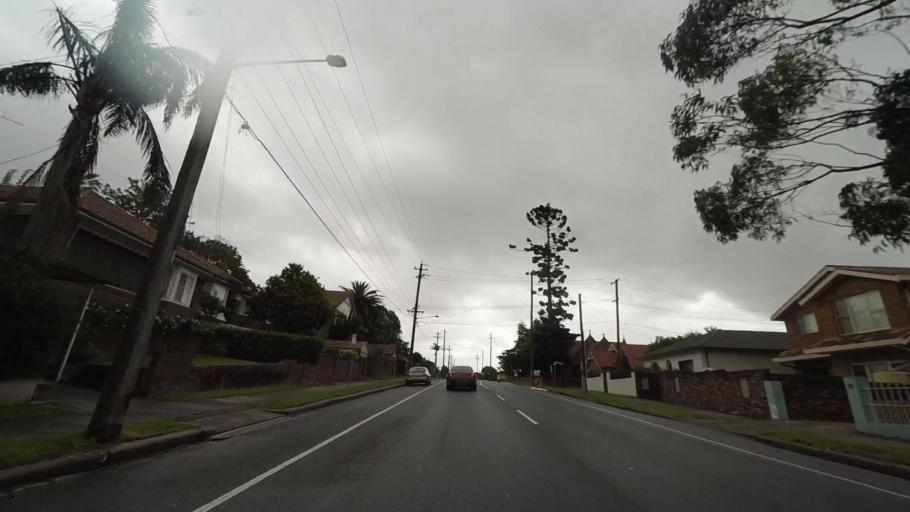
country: AU
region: New South Wales
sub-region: Kogarah
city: Kogarah Bay
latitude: -33.9771
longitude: 151.1211
